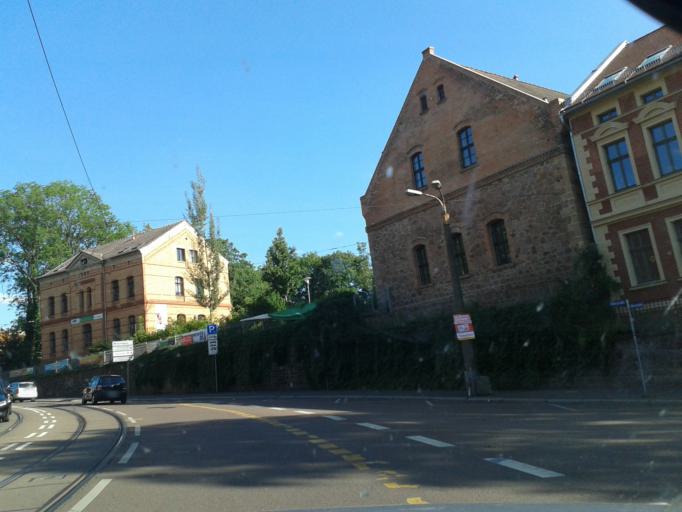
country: DE
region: Saxony-Anhalt
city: Sennewitz
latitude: 51.5025
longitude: 11.9530
